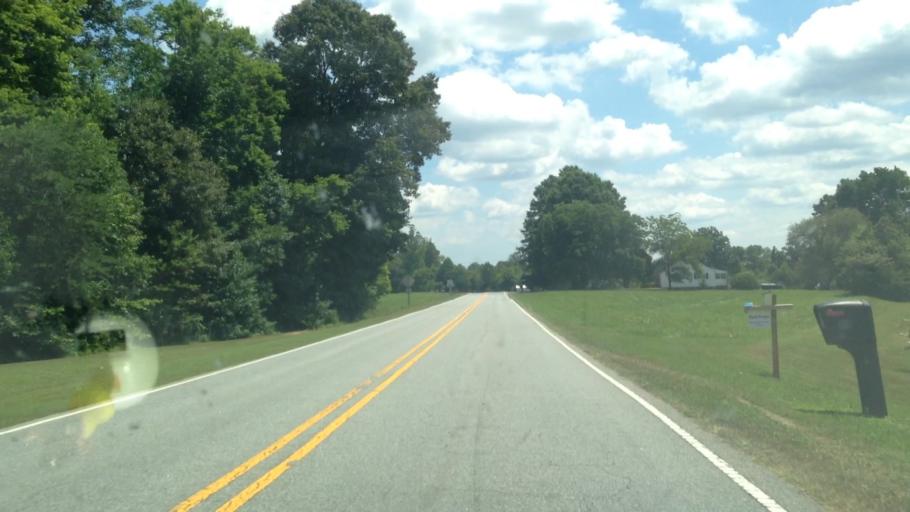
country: US
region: North Carolina
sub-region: Guilford County
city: Oak Ridge
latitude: 36.1792
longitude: -80.0392
